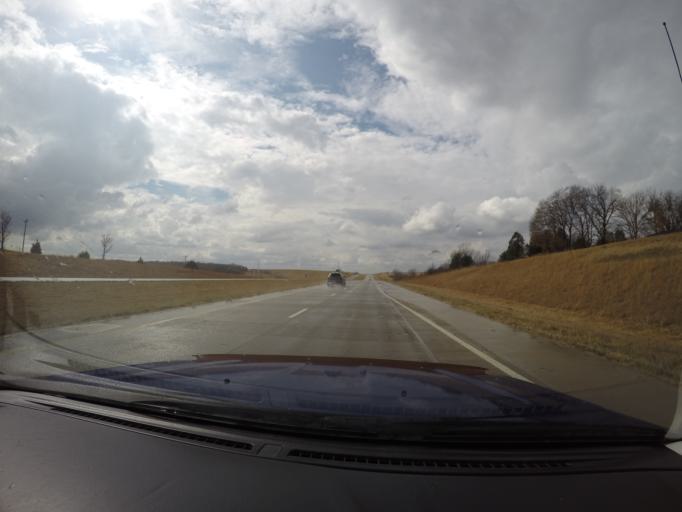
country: US
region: Kansas
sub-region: Pottawatomie County
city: Wamego
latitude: 39.2104
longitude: -96.3714
